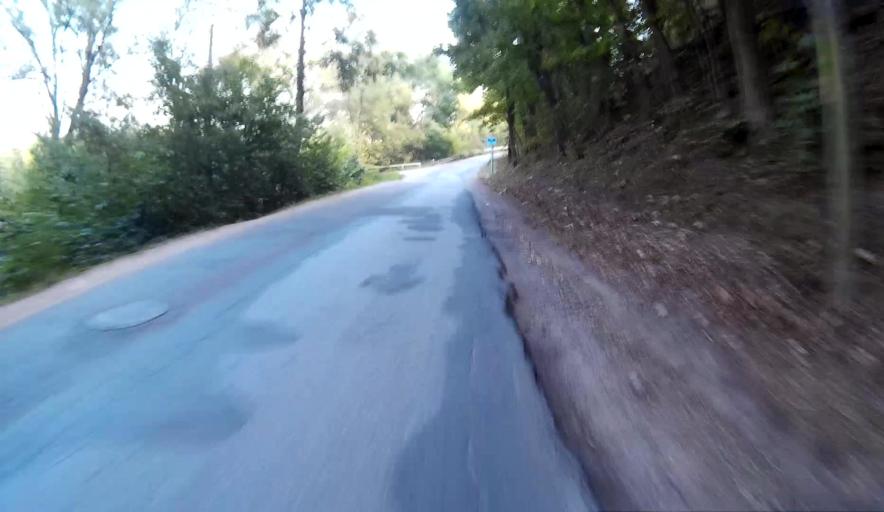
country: CZ
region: South Moravian
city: Podoli
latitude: 49.1945
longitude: 16.7194
